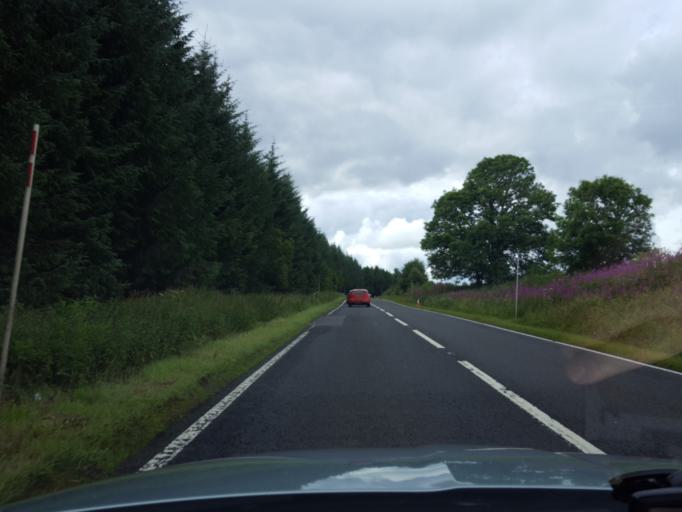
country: GB
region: Scotland
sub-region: Moray
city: Rothes
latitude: 57.4355
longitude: -3.3033
